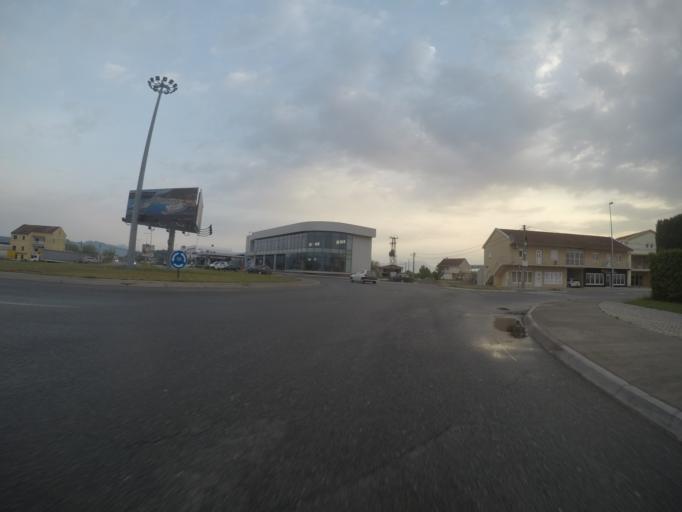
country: ME
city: Mojanovici
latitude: 42.3666
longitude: 19.2272
